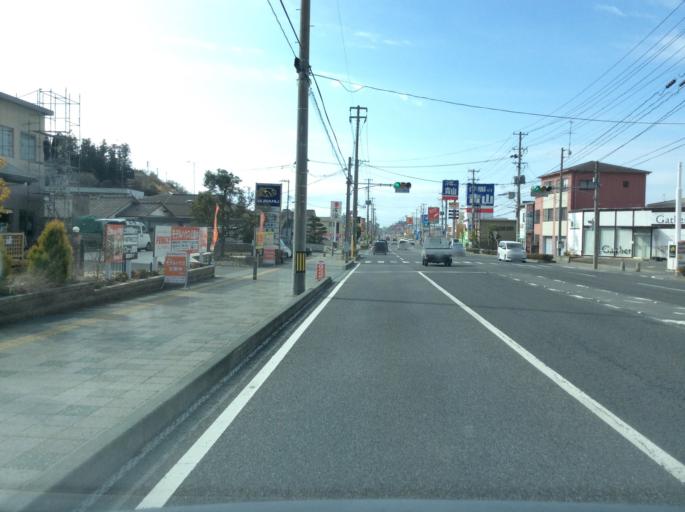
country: JP
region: Fukushima
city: Iwaki
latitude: 36.9685
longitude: 140.9051
